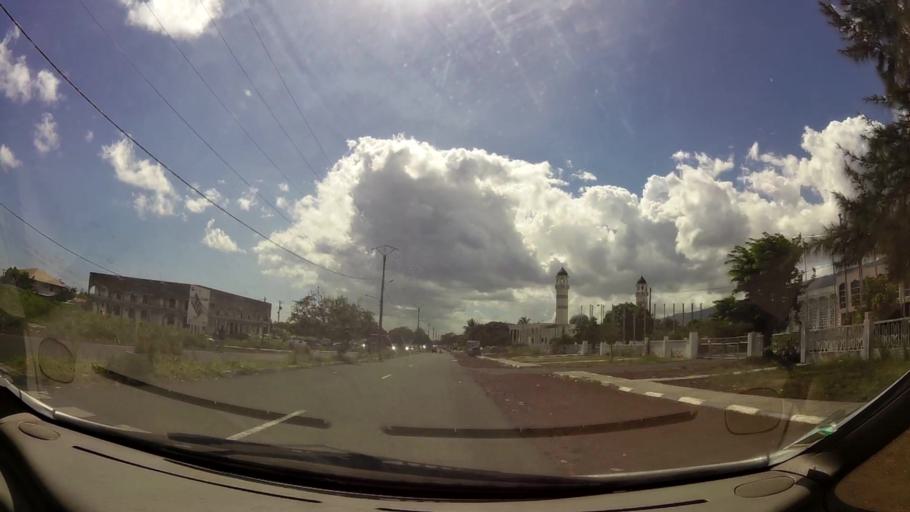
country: KM
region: Grande Comore
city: Mavingouni
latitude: -11.7186
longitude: 43.2453
